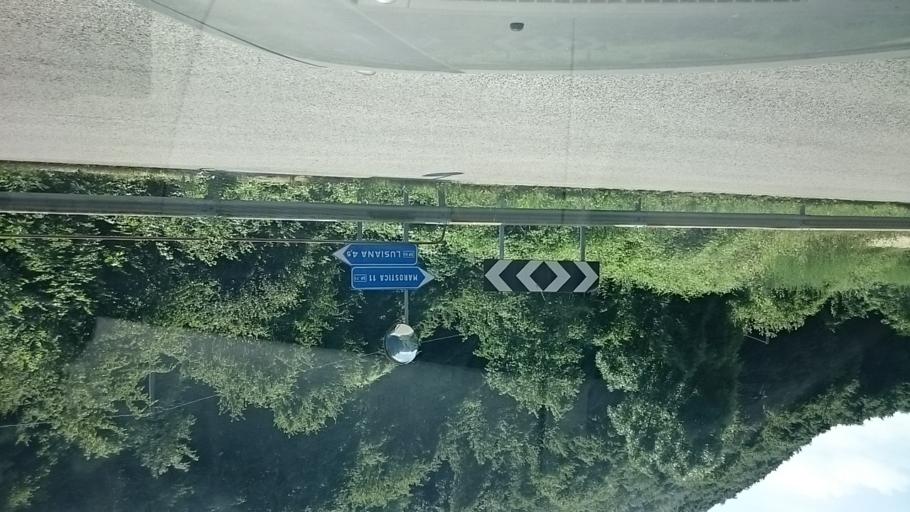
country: IT
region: Veneto
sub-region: Provincia di Vicenza
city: Conco
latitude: 45.7844
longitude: 11.5989
